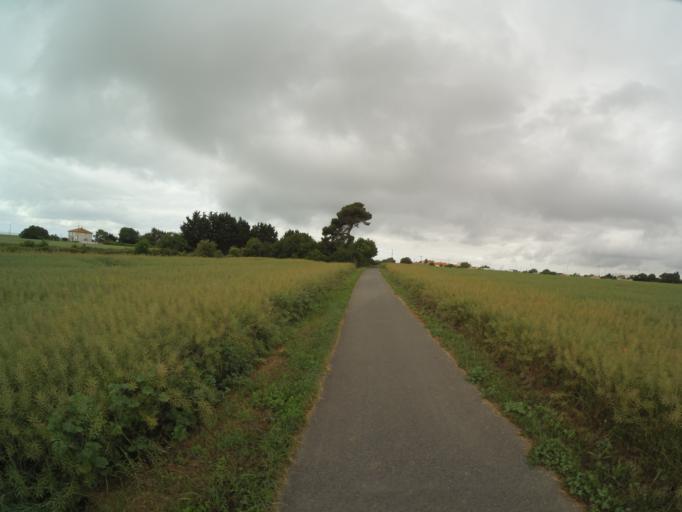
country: FR
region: Poitou-Charentes
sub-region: Departement de la Charente-Maritime
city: Aytre
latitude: 46.1317
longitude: -1.1351
